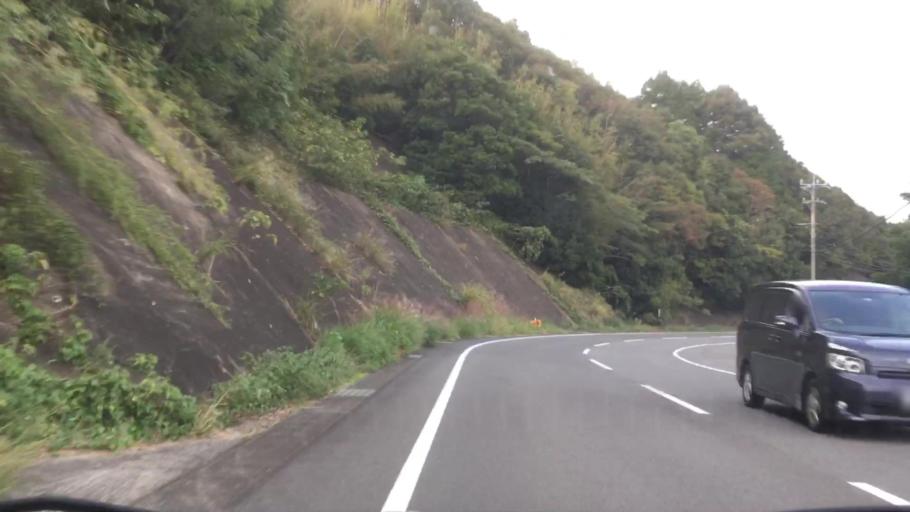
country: JP
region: Nagasaki
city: Sasebo
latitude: 32.9531
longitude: 129.6747
